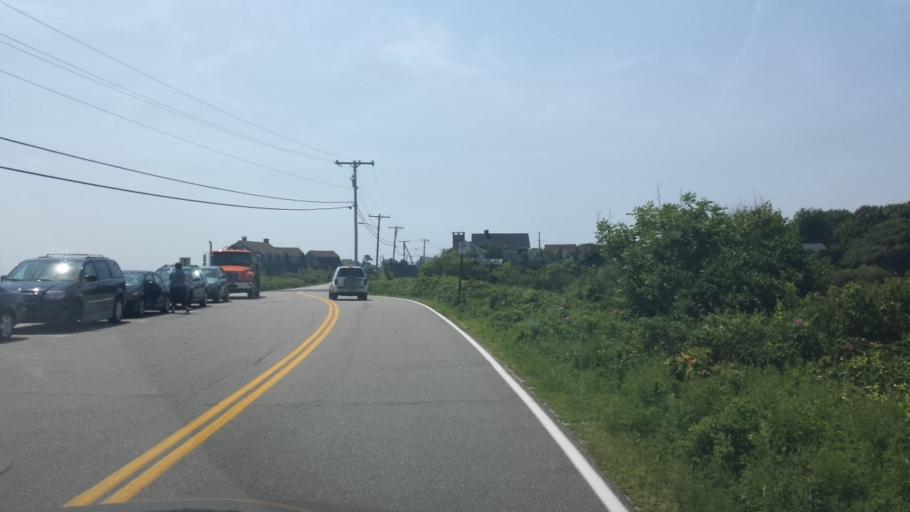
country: US
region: Maine
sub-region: York County
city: Old Orchard Beach
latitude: 43.4272
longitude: -70.3775
